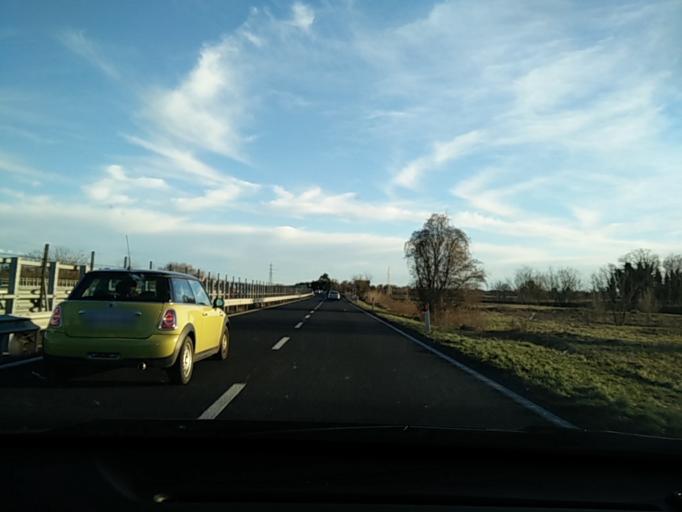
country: IT
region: Friuli Venezia Giulia
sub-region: Provincia di Udine
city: Passons
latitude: 46.0620
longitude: 13.1980
